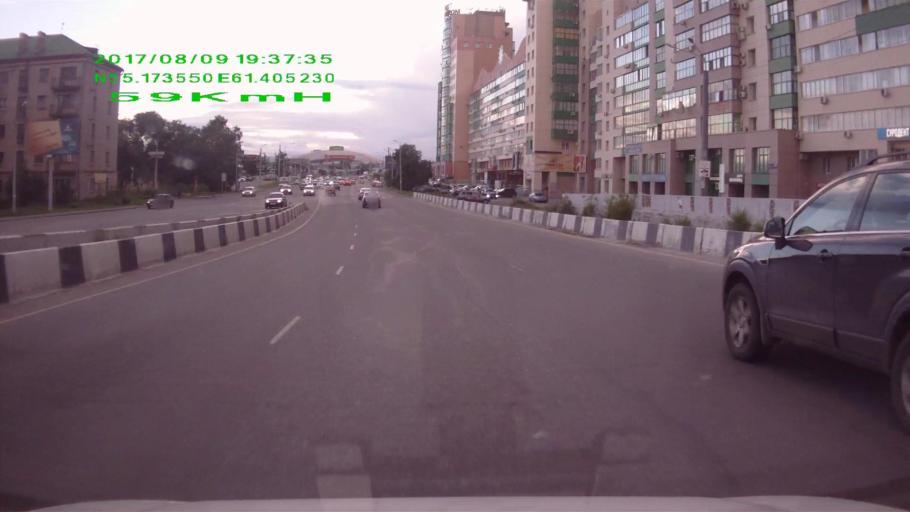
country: RU
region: Chelyabinsk
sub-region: Gorod Chelyabinsk
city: Chelyabinsk
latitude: 55.1735
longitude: 61.4040
